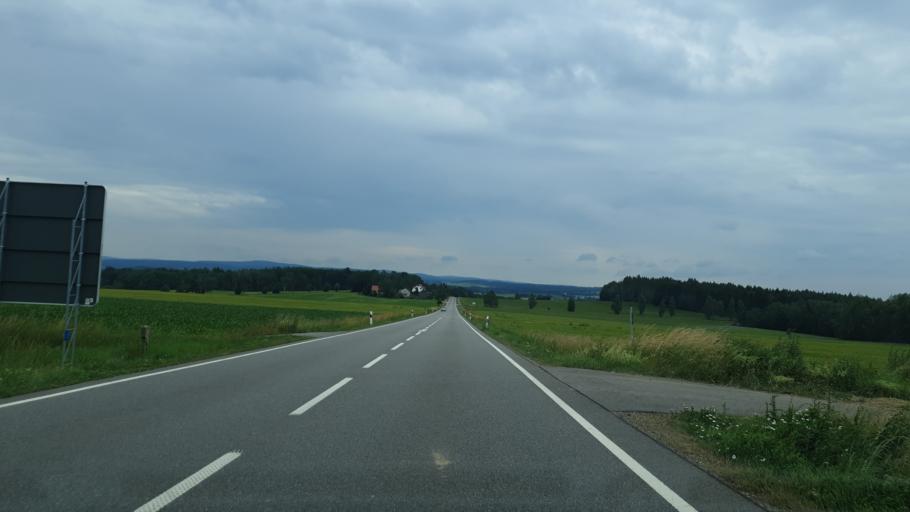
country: DE
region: Saxony
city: Hirschfeld
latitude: 50.6320
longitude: 12.4314
